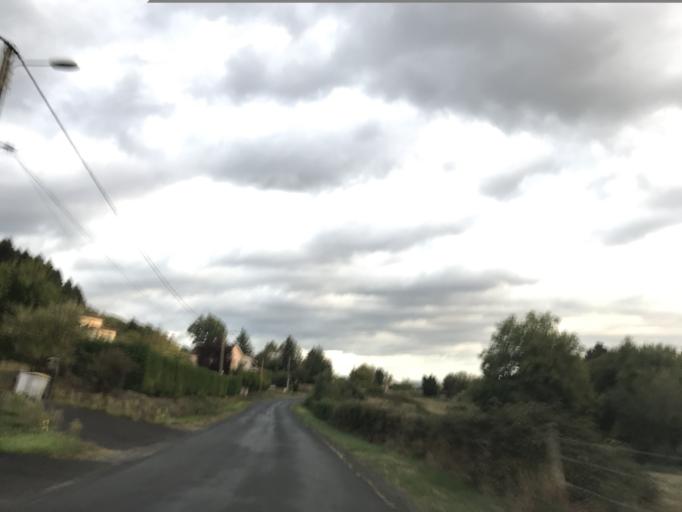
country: FR
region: Auvergne
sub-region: Departement du Puy-de-Dome
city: Escoutoux
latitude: 45.8289
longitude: 3.5518
